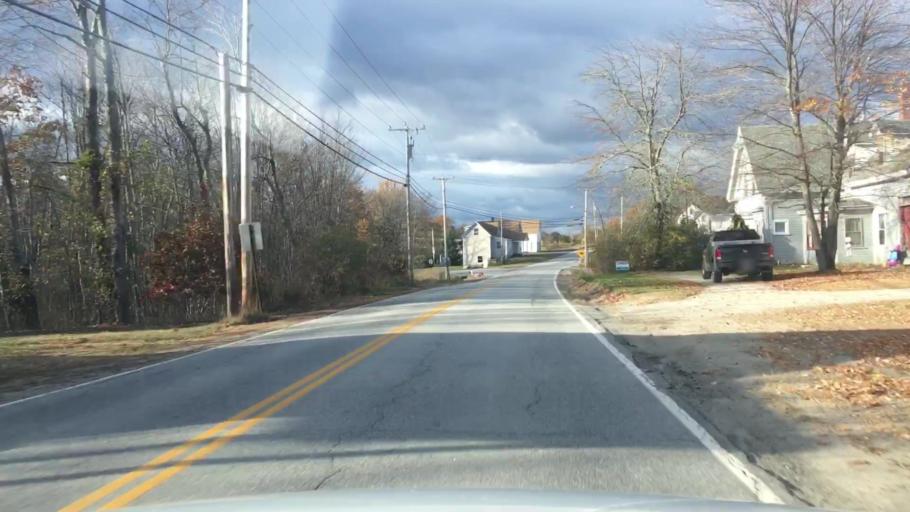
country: US
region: Maine
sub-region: Androscoggin County
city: Leeds
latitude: 44.3025
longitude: -70.1186
